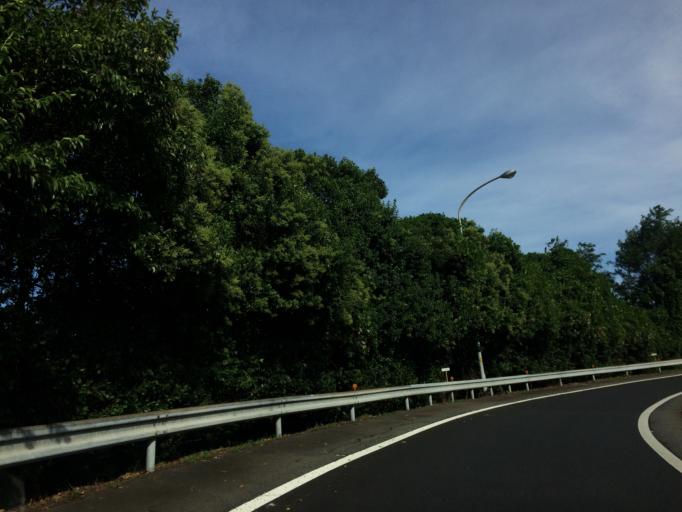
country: JP
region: Gunma
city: Shibukawa
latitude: 36.4795
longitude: 139.0176
